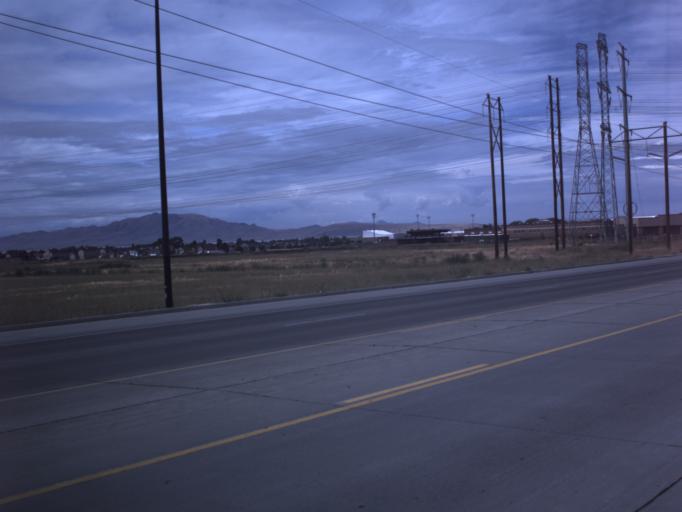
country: US
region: Utah
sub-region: Davis County
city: Clearfield
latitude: 41.1107
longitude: -112.0504
